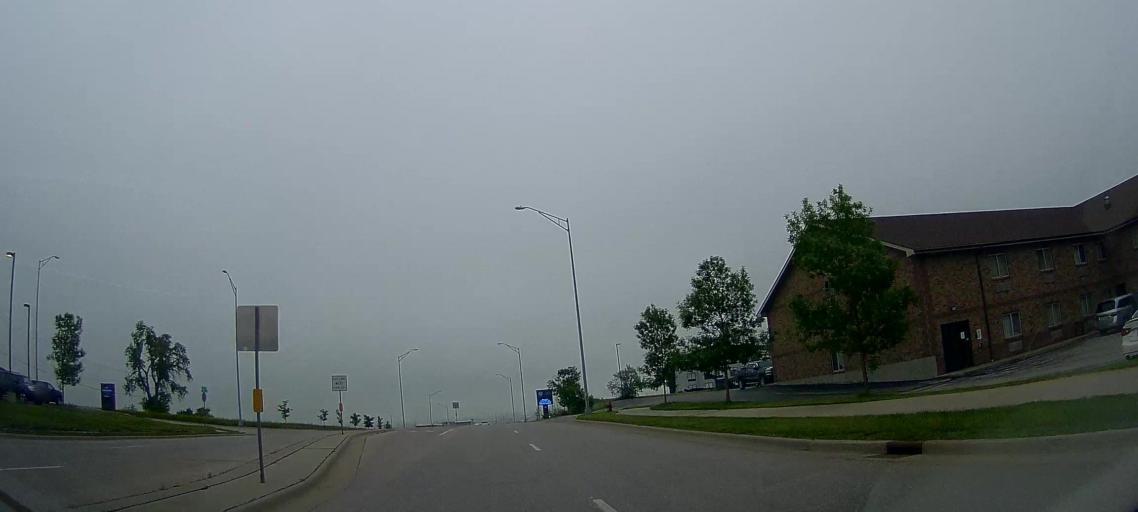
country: US
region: South Dakota
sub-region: Pennington County
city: Rapid City
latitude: 44.1008
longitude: -103.2007
